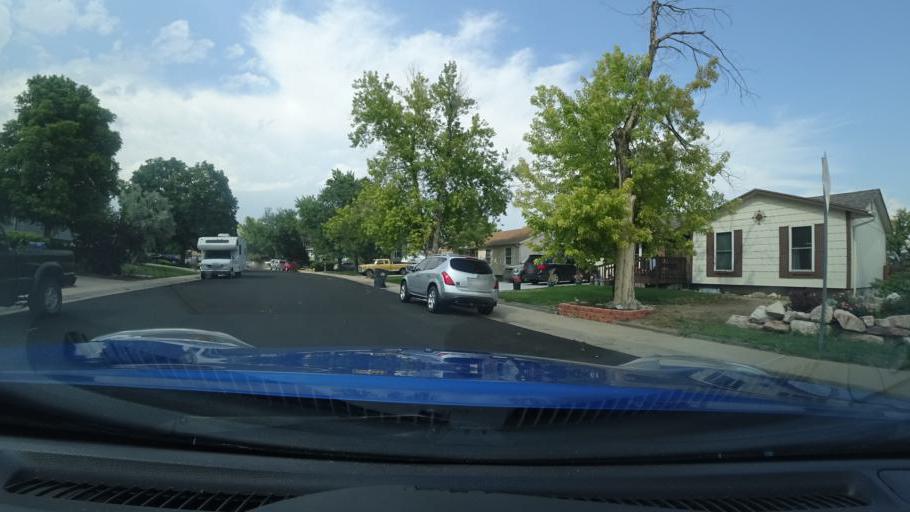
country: US
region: Colorado
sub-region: Adams County
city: Aurora
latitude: 39.6855
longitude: -104.7847
